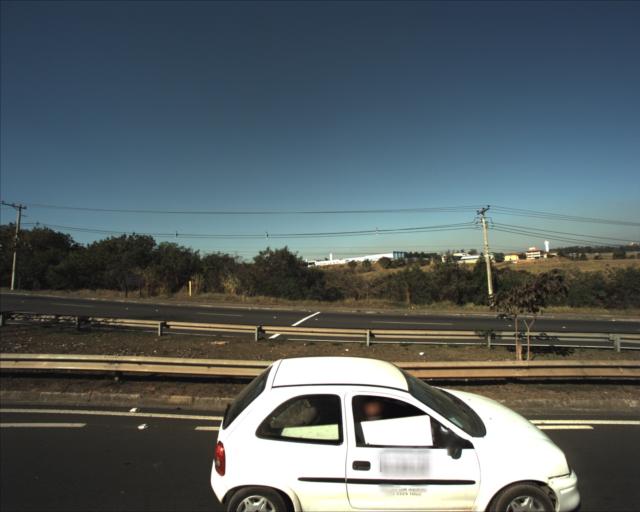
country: BR
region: Sao Paulo
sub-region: Sorocaba
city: Sorocaba
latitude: -23.4628
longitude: -47.4230
